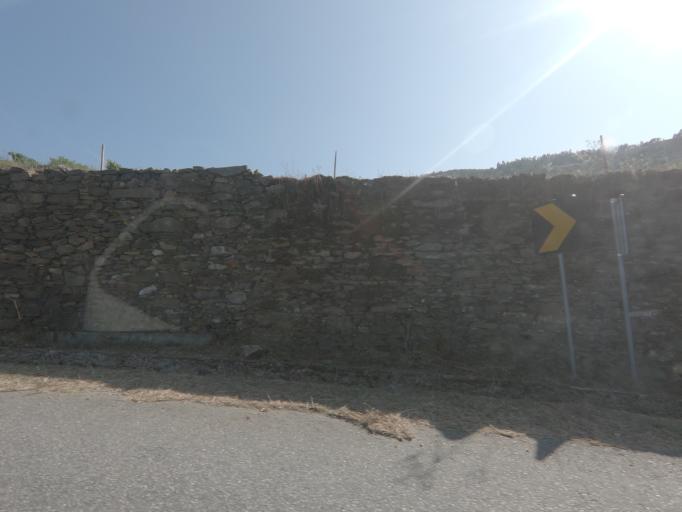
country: PT
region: Vila Real
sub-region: Sabrosa
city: Vilela
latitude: 41.2345
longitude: -7.5724
